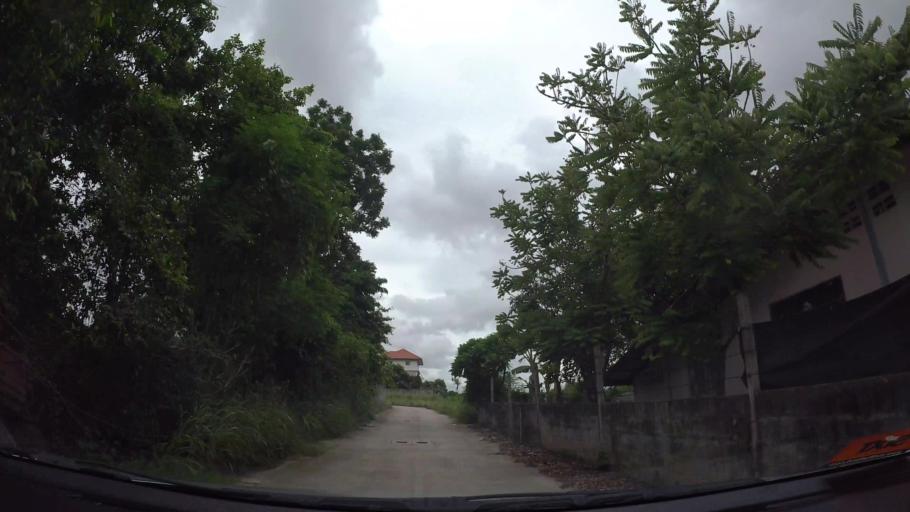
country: TH
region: Chon Buri
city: Si Racha
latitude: 13.1791
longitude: 100.9776
